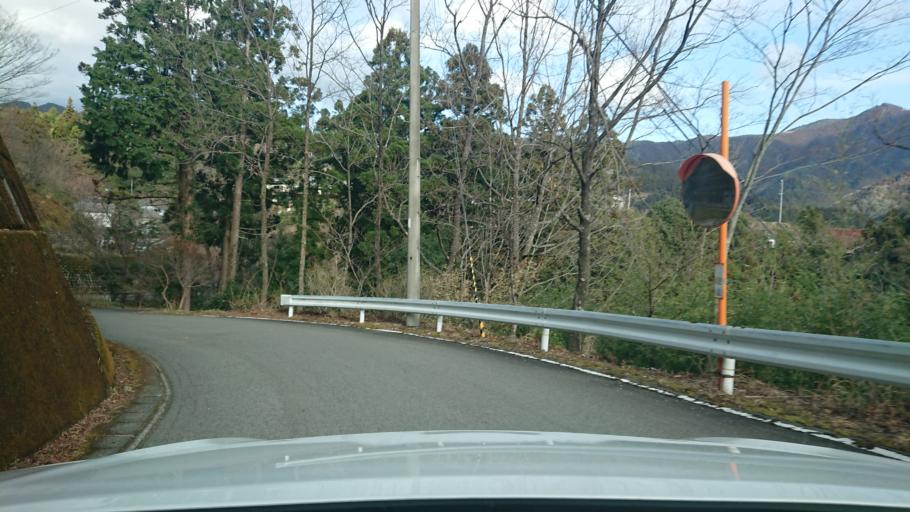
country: JP
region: Tokushima
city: Ishii
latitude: 33.9142
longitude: 134.4075
